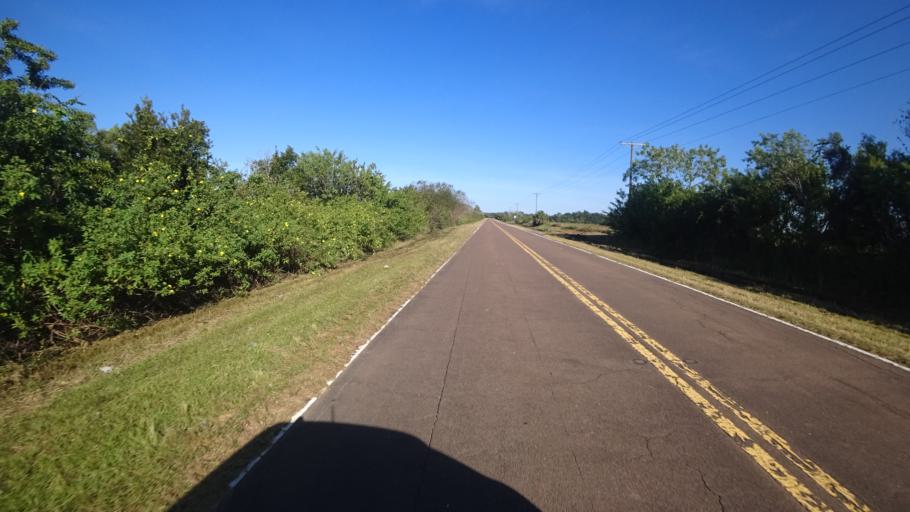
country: US
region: Florida
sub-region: Hillsborough County
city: Ruskin
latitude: 27.6517
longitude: -82.4298
